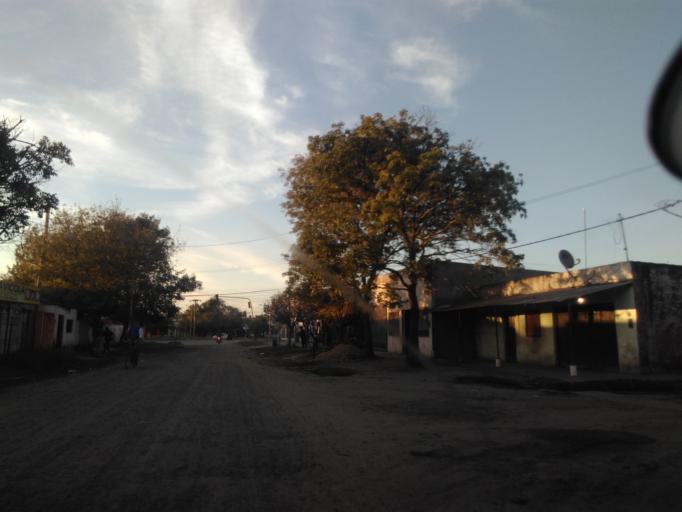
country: AR
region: Chaco
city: Resistencia
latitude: -27.4793
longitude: -58.9907
